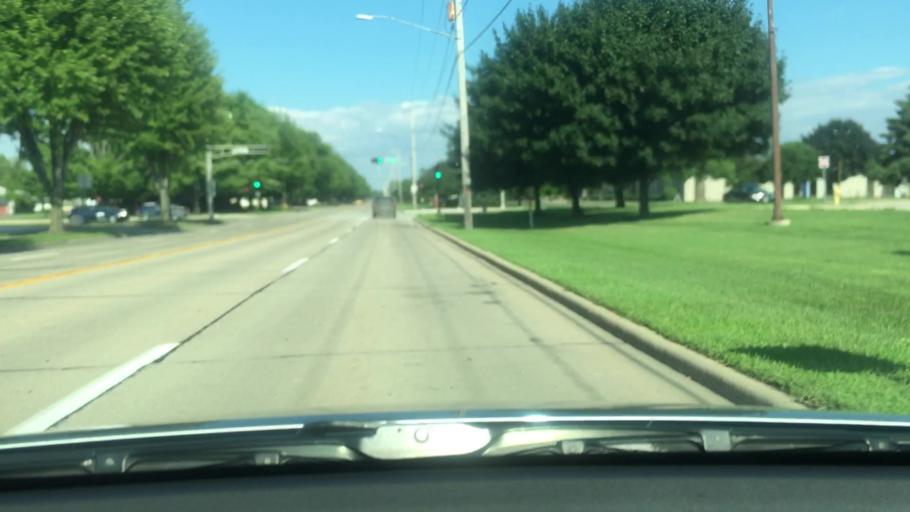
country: US
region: Wisconsin
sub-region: Winnebago County
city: Oshkosh
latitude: 43.9959
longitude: -88.5637
